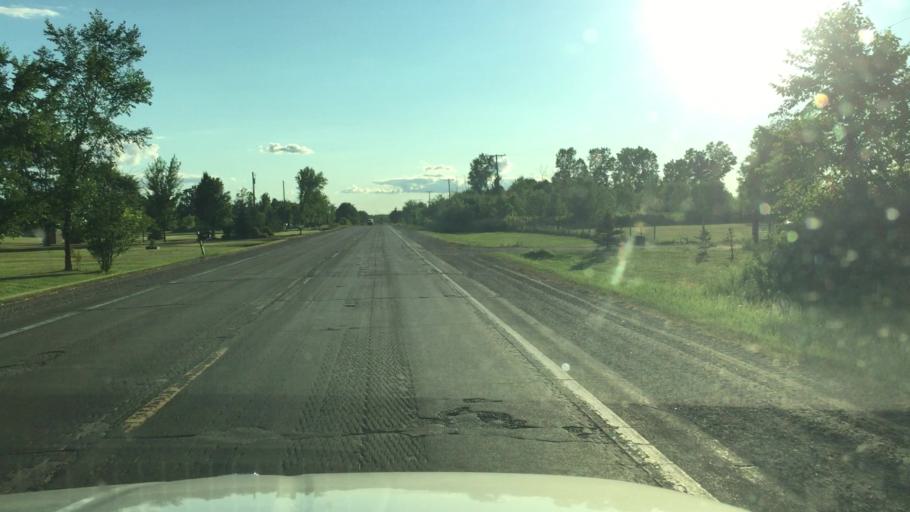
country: US
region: Michigan
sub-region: Saint Clair County
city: Capac
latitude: 43.0258
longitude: -82.9920
